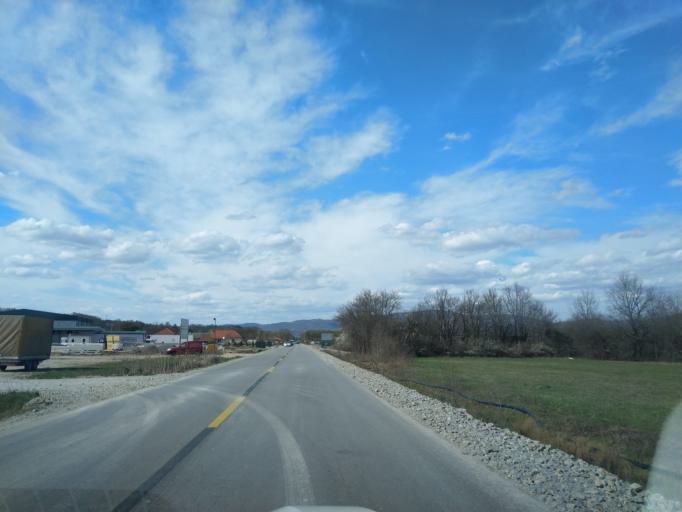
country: RS
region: Central Serbia
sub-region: Zlatiborski Okrug
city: Arilje
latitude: 43.7986
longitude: 20.0970
